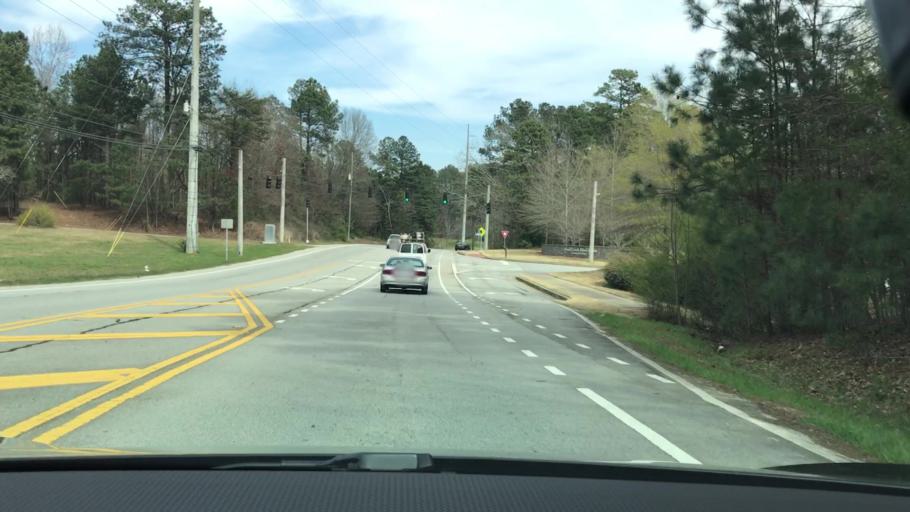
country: US
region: Georgia
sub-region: Gwinnett County
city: Sugar Hill
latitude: 34.1504
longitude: -84.0431
